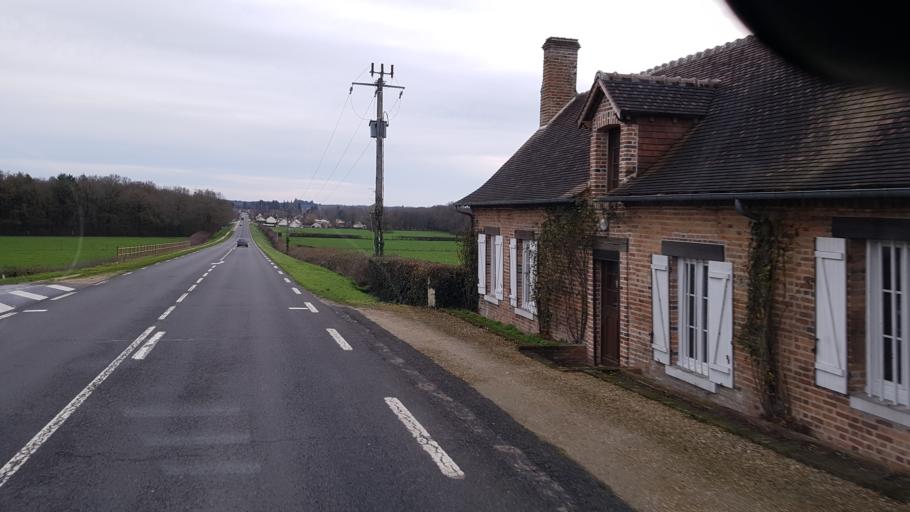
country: FR
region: Centre
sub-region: Departement du Loir-et-Cher
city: Lamotte-Beuvron
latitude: 47.6168
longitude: 2.0160
